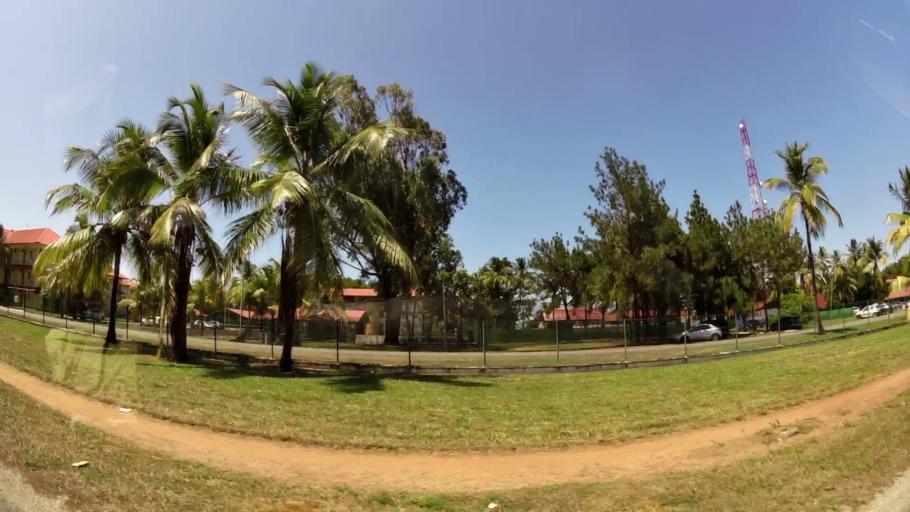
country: GF
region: Guyane
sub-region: Guyane
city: Kourou
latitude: 5.1710
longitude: -52.6486
